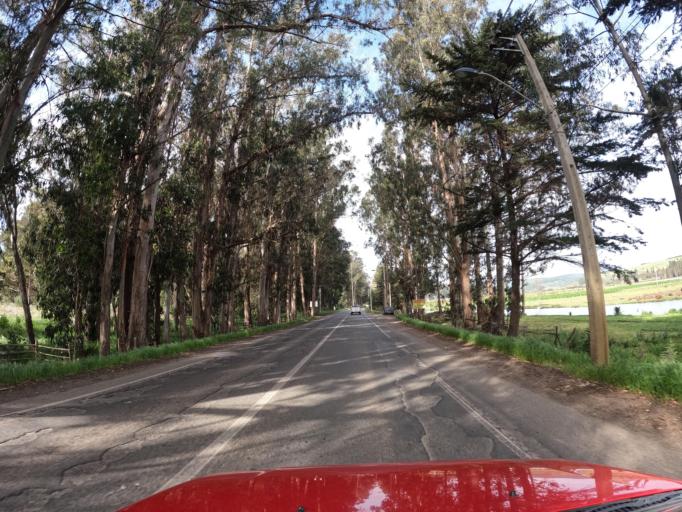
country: CL
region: O'Higgins
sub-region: Provincia de Colchagua
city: Santa Cruz
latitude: -34.3847
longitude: -71.9841
